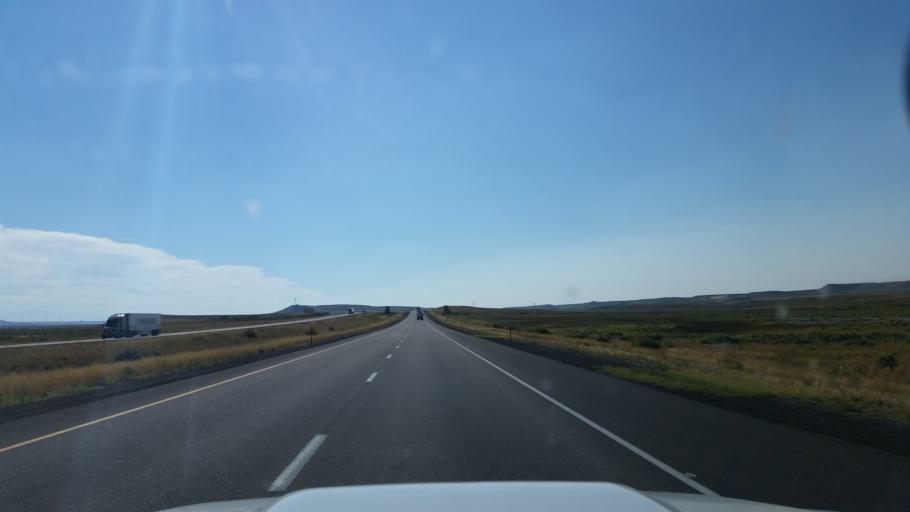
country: US
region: Wyoming
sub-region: Uinta County
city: Lyman
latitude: 41.3550
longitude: -110.3564
